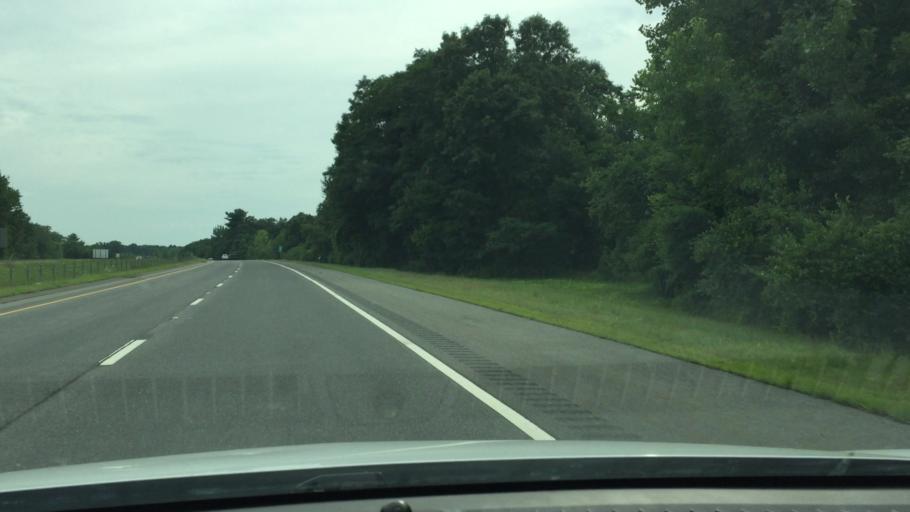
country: US
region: Massachusetts
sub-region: Hampden County
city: Agawam
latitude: 42.0689
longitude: -72.6474
